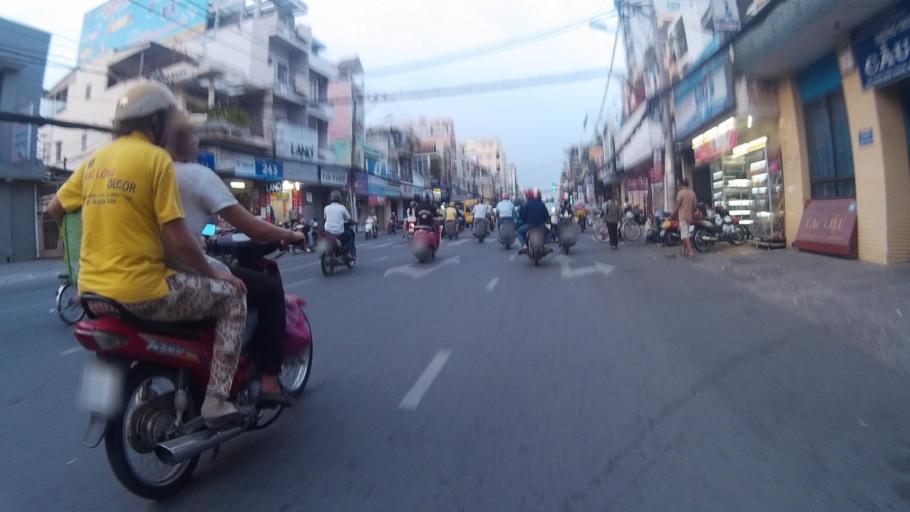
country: VN
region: Ho Chi Minh City
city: Quan Phu Nhuan
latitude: 10.7963
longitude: 106.6817
